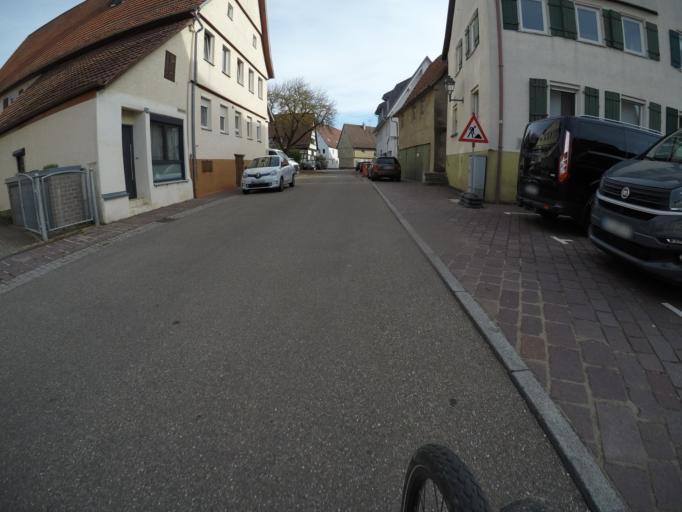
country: DE
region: Baden-Wuerttemberg
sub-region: Regierungsbezirk Stuttgart
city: Weil der Stadt
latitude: 48.7689
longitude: 8.8544
